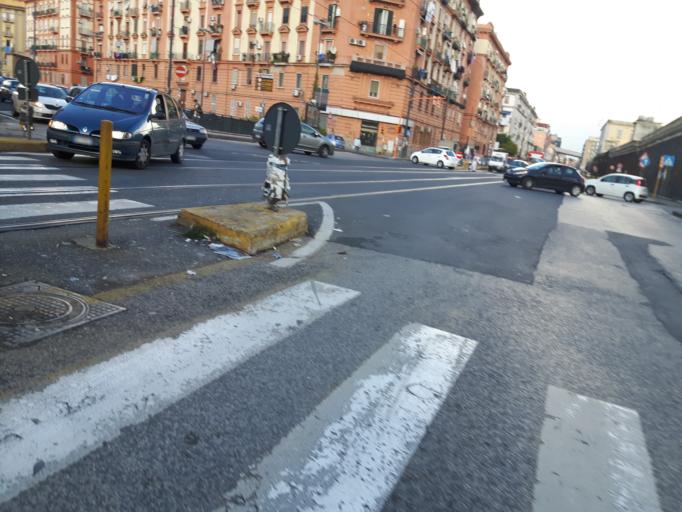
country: IT
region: Campania
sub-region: Provincia di Napoli
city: Napoli
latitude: 40.8594
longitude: 14.2761
